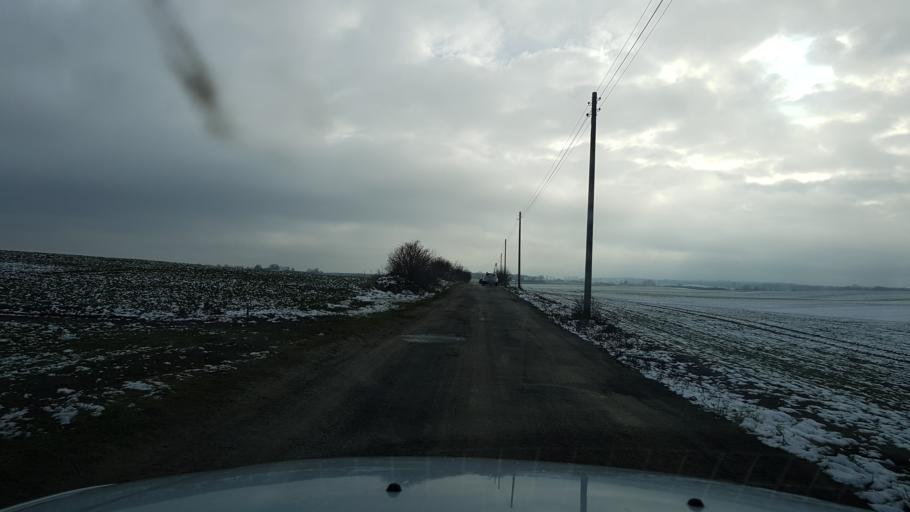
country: PL
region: West Pomeranian Voivodeship
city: Trzcinsko Zdroj
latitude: 52.9609
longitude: 14.6765
